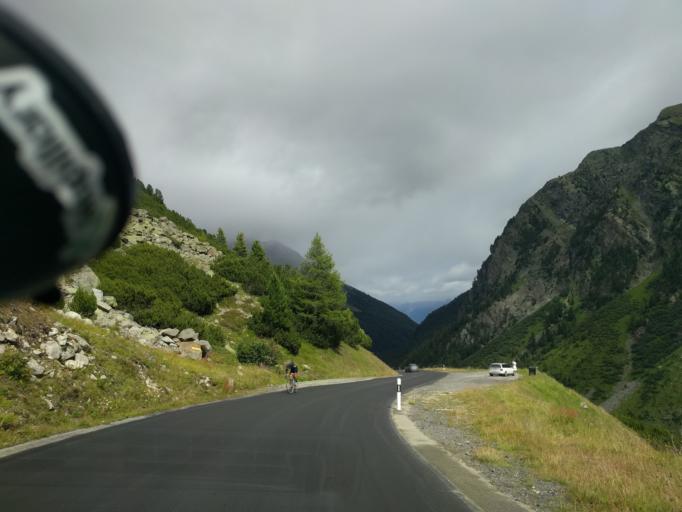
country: CH
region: Grisons
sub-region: Inn District
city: Zernez
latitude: 46.7459
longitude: 9.9931
